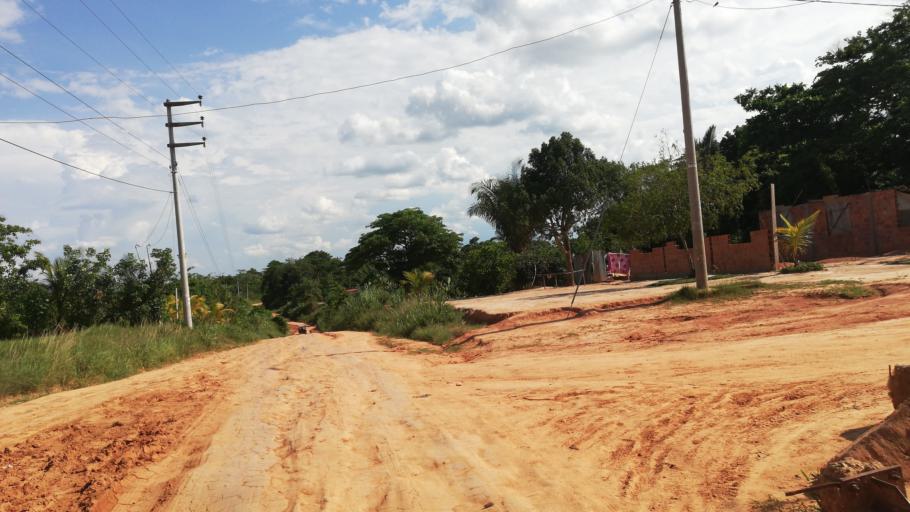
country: PE
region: Ucayali
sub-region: Provincia de Coronel Portillo
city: Puerto Callao
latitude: -8.2706
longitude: -74.6481
